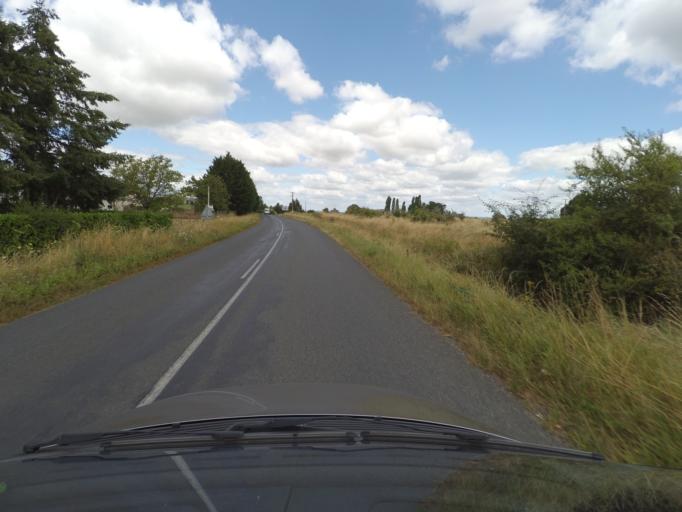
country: FR
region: Pays de la Loire
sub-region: Departement de Maine-et-Loire
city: Gennes
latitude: 47.3302
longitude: -0.2363
